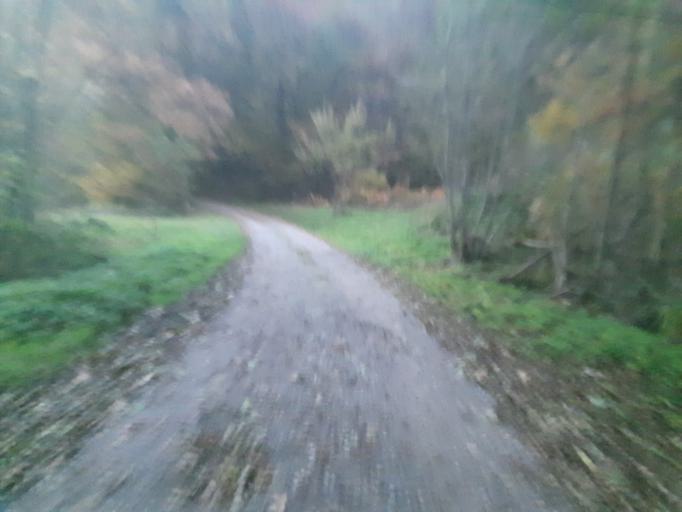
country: DE
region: Bavaria
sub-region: Regierungsbezirk Unterfranken
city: Leidersbach
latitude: 49.8976
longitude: 9.2509
